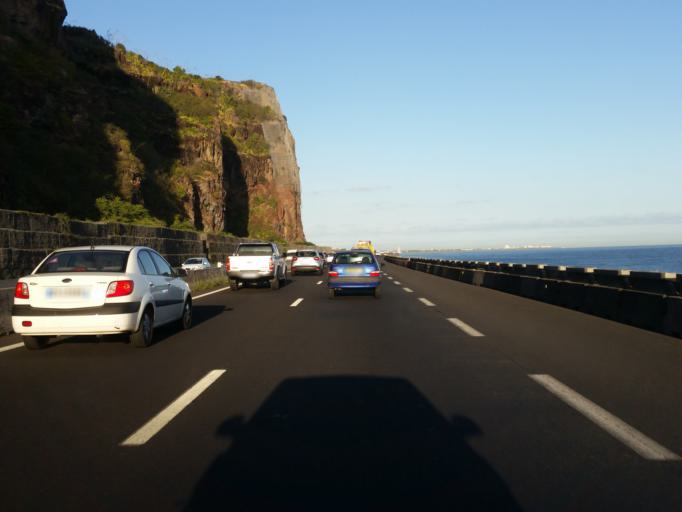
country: RE
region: Reunion
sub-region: Reunion
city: La Possession
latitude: -20.9101
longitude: 55.3556
